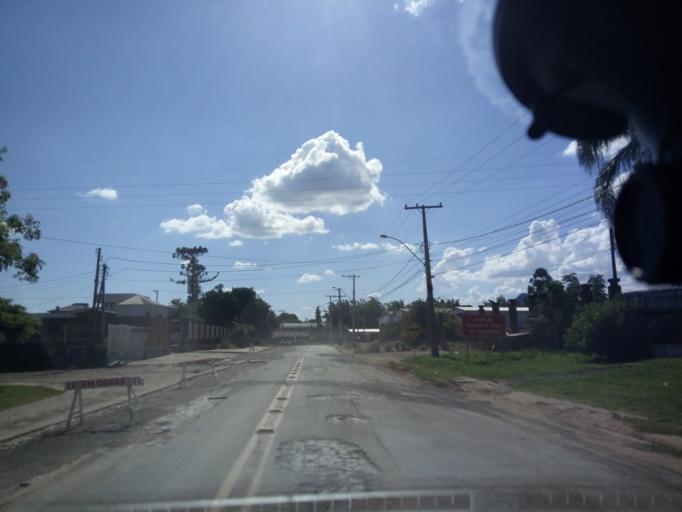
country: BR
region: Rio Grande do Sul
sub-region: Santa Maria
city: Santa Maria
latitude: -29.6978
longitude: -53.7298
